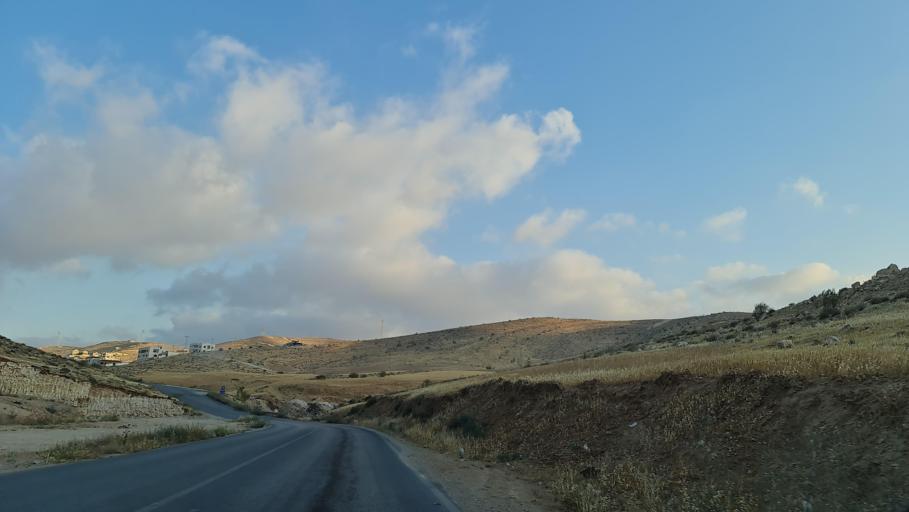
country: JO
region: Zarqa
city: Zarqa
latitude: 32.0821
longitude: 36.0348
